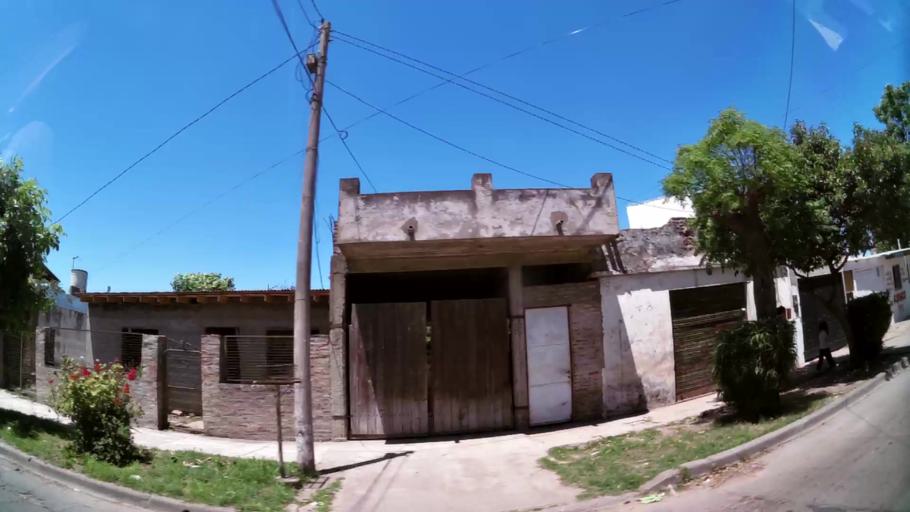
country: AR
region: Buenos Aires
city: Hurlingham
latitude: -34.5034
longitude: -58.7030
